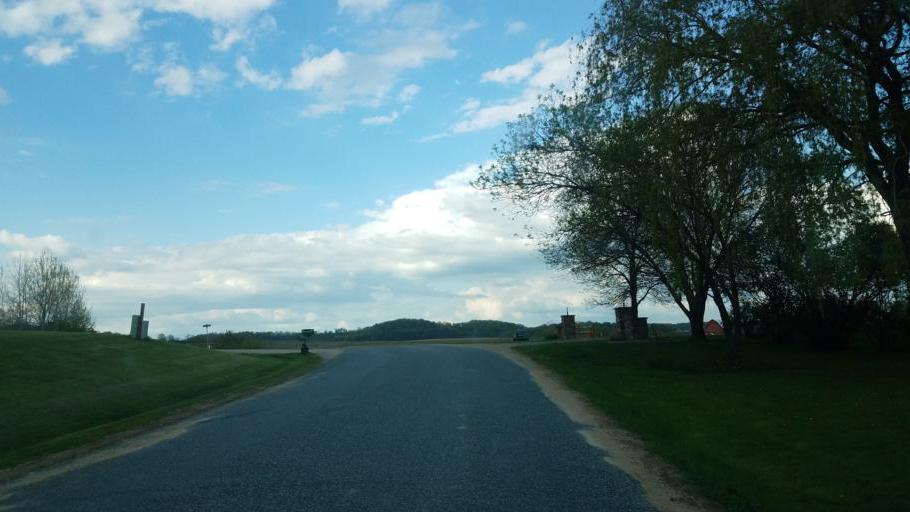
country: US
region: Wisconsin
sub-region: Vernon County
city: Hillsboro
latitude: 43.6607
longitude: -90.3842
